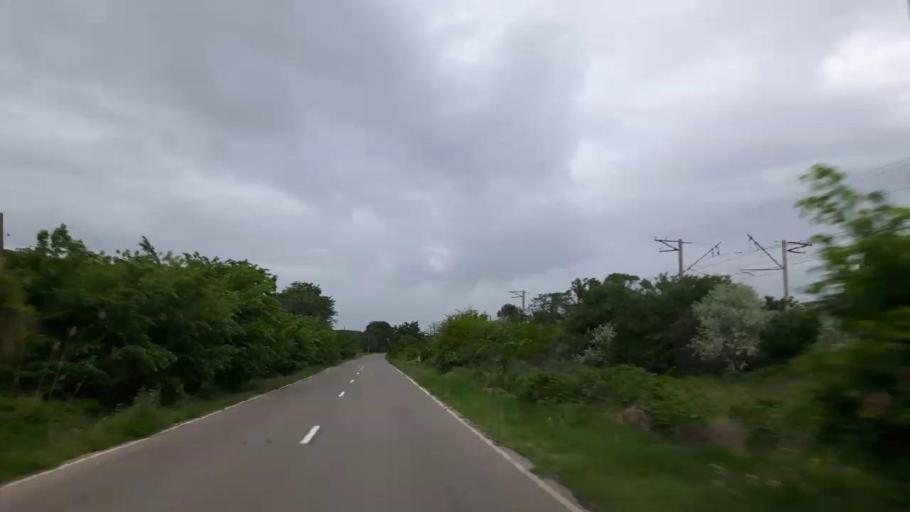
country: GE
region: Shida Kartli
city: Gori
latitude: 41.9936
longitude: 44.0296
